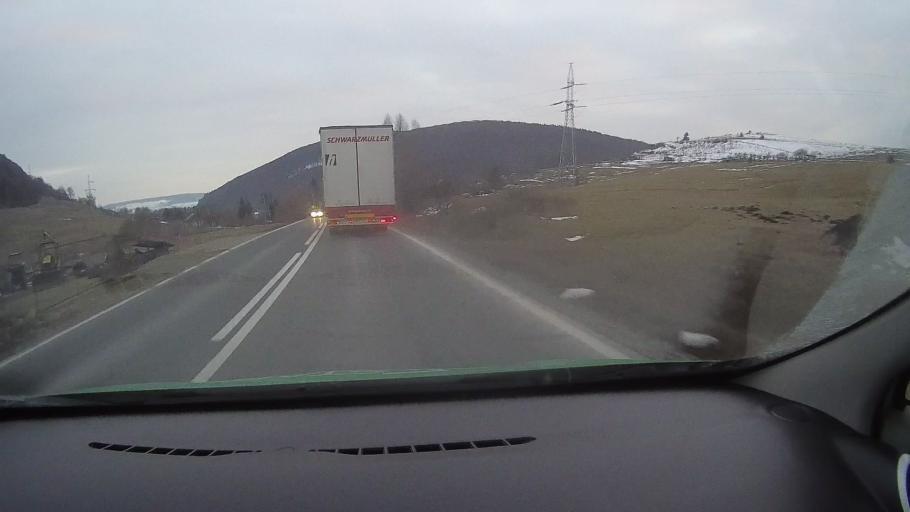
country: RO
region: Harghita
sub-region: Municipiul Odorheiu Secuiesc
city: Odorheiu Secuiesc
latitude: 46.3385
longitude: 25.2698
